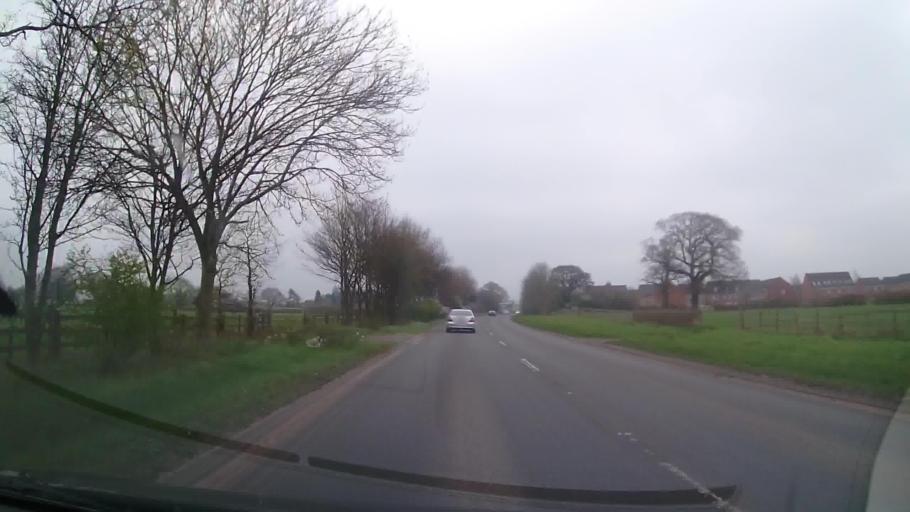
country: GB
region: England
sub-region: Shropshire
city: Market Drayton
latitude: 52.9119
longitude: -2.4961
